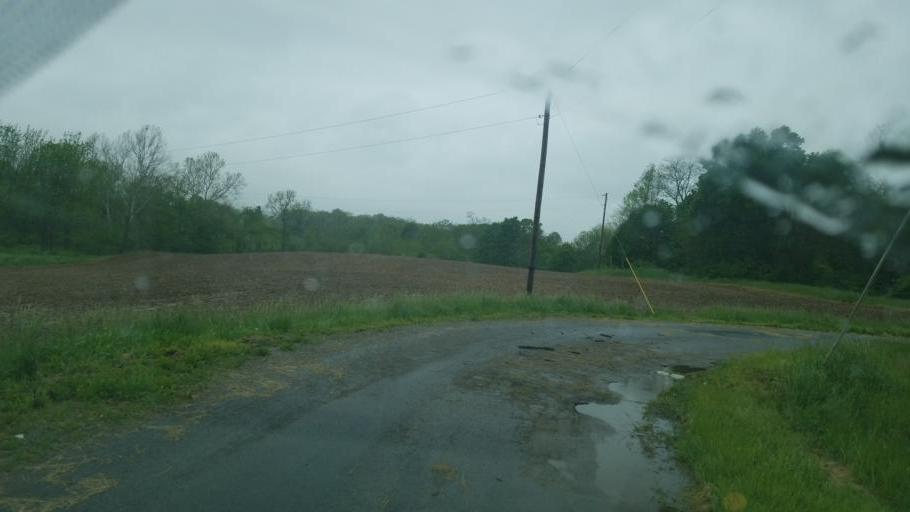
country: US
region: Ohio
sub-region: Highland County
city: Greenfield
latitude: 39.3285
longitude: -83.4499
